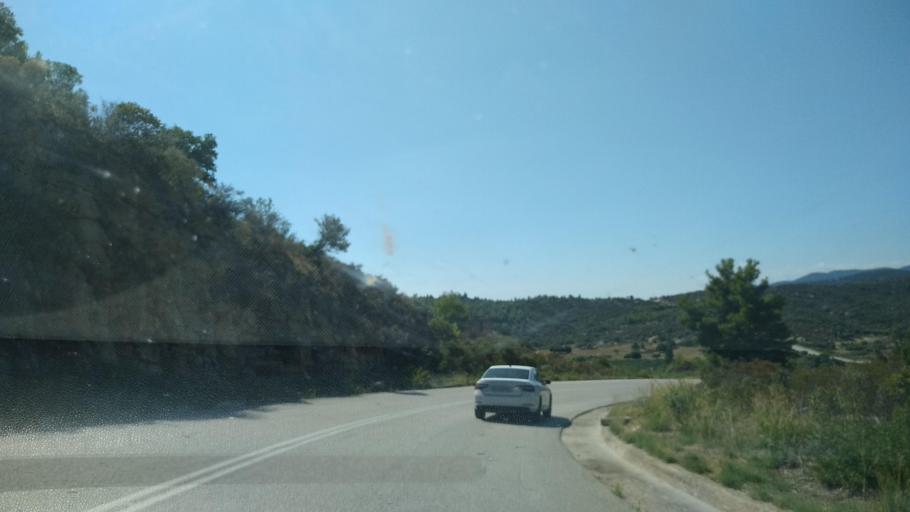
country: GR
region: Central Macedonia
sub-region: Nomos Chalkidikis
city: Sykia
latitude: 39.9901
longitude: 23.9052
